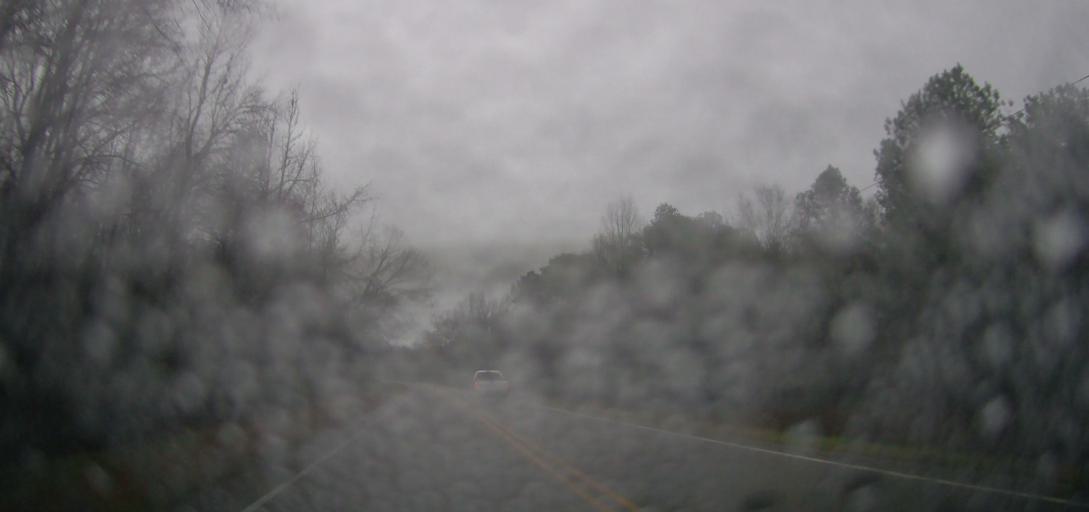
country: US
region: Alabama
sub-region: Autauga County
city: Prattville
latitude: 32.4913
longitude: -86.5716
